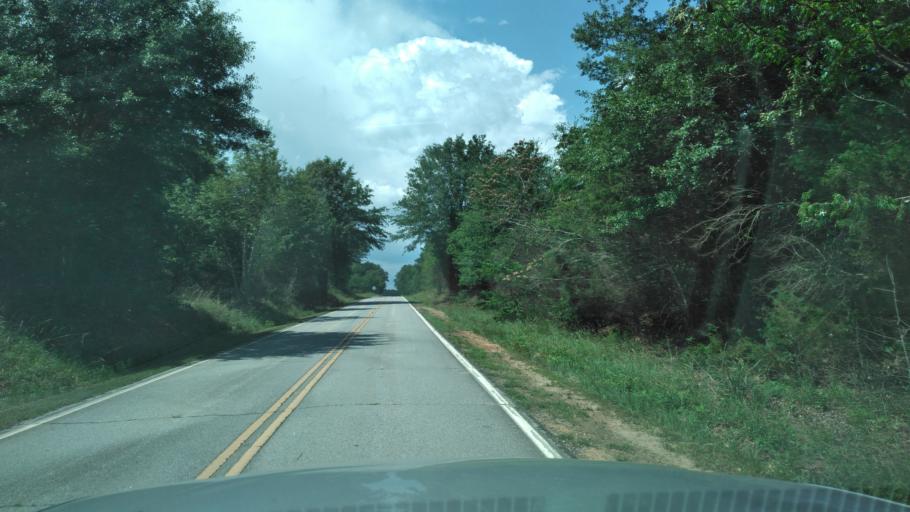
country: US
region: South Carolina
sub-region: Laurens County
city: Laurens
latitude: 34.4961
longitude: -82.0939
